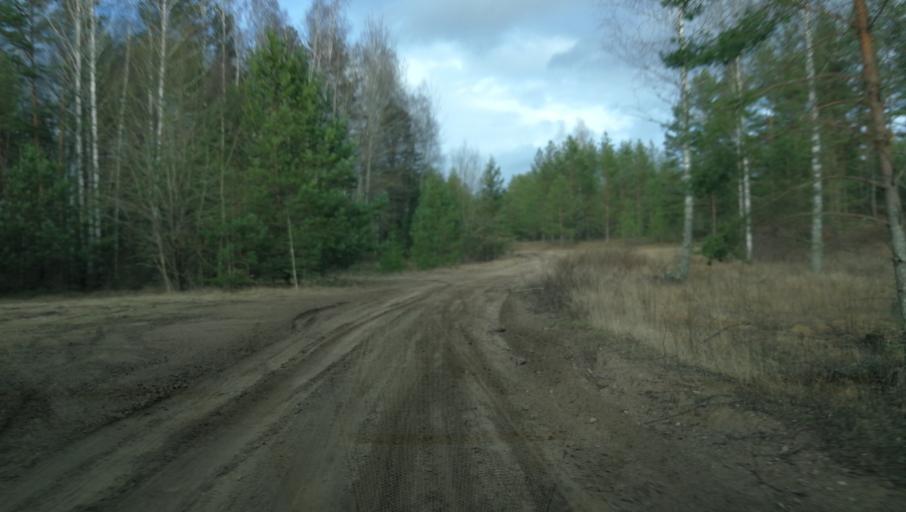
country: LV
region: Adazi
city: Adazi
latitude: 57.0583
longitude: 24.2584
